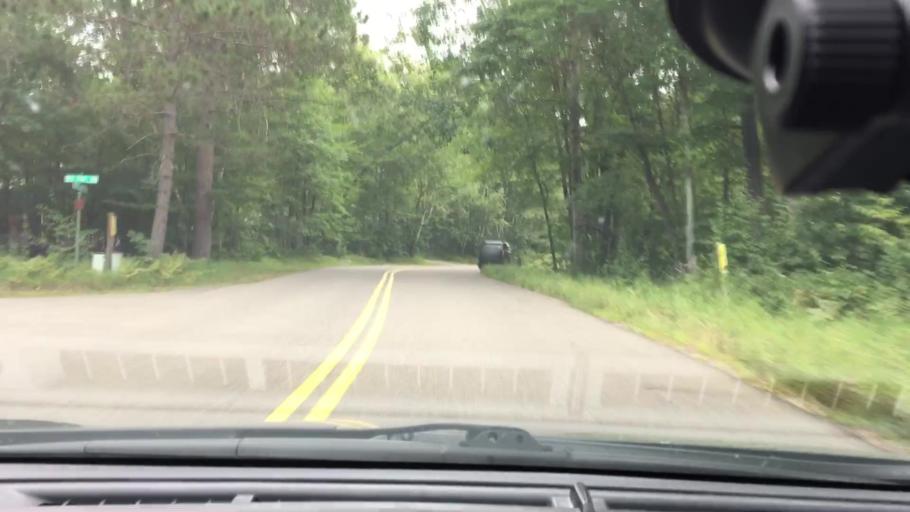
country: US
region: Minnesota
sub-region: Crow Wing County
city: Cross Lake
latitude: 46.6720
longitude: -94.0393
